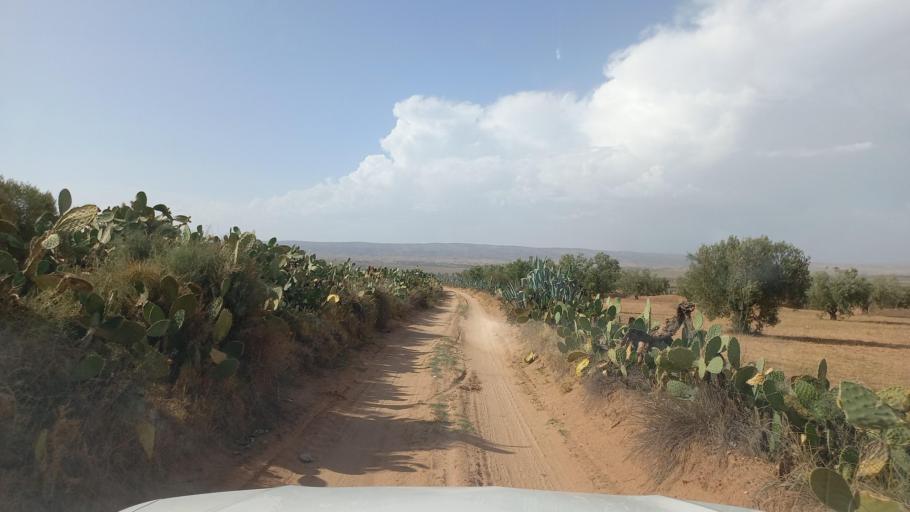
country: TN
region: Al Qasrayn
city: Kasserine
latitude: 35.2071
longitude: 8.9680
